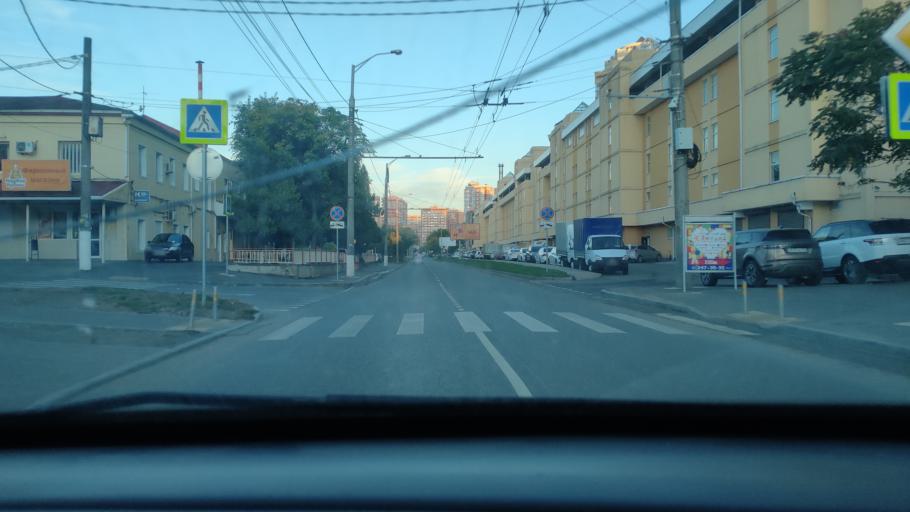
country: RU
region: Krasnodarskiy
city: Krasnodar
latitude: 45.0384
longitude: 38.9409
